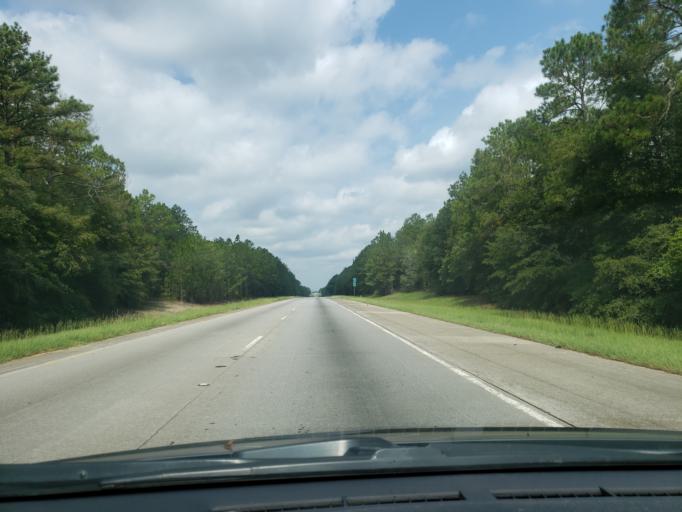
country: US
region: Georgia
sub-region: Emanuel County
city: Swainsboro
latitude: 32.4116
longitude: -82.3628
